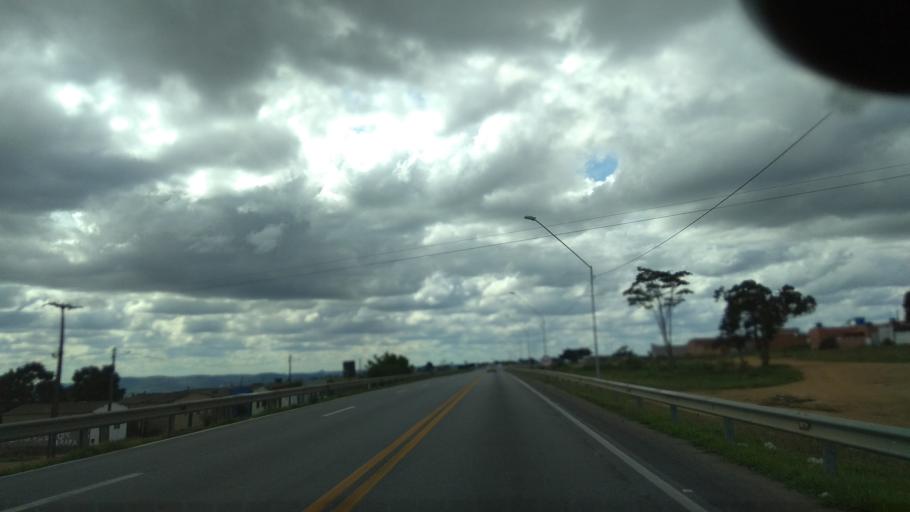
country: BR
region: Bahia
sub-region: Santa Ines
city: Santa Ines
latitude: -13.0709
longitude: -39.9611
